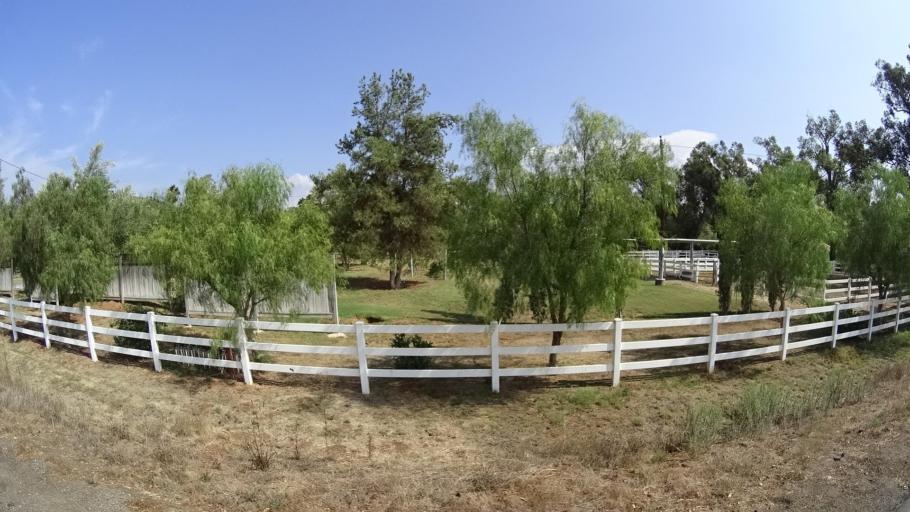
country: US
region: California
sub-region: San Diego County
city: Escondido
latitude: 33.1154
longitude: -117.0443
